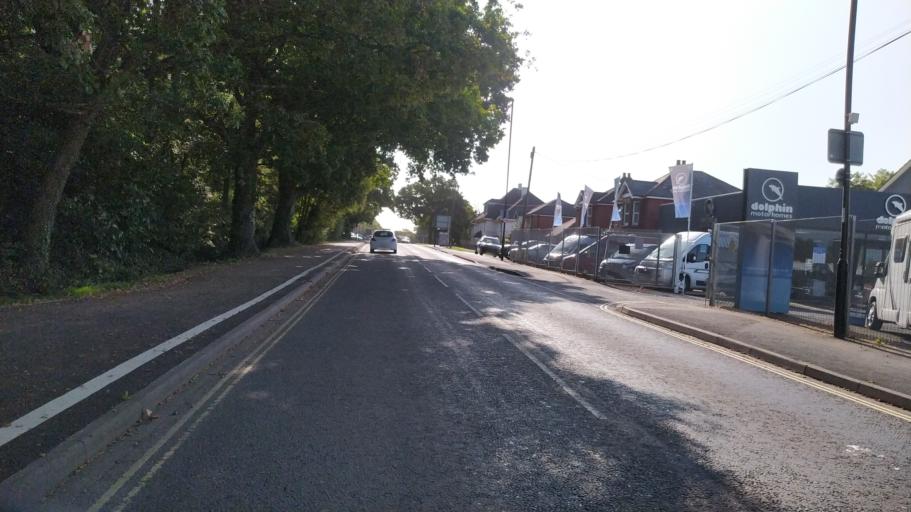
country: GB
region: England
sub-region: Hampshire
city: Bursledon
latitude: 50.9008
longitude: -1.3303
